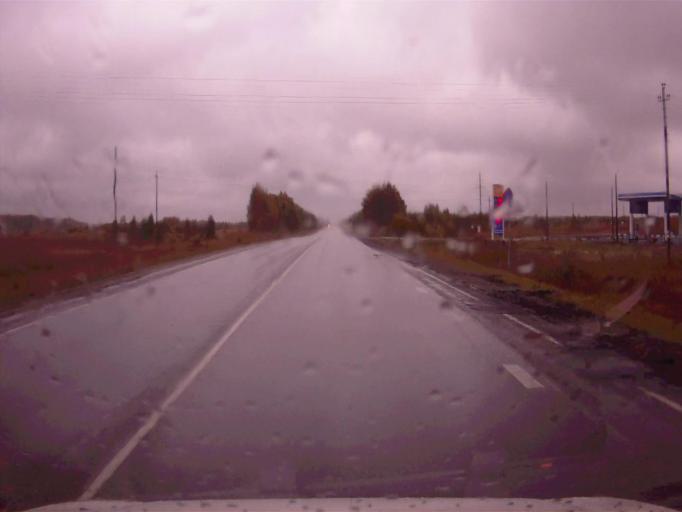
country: RU
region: Chelyabinsk
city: Argayash
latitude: 55.4777
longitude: 60.8527
